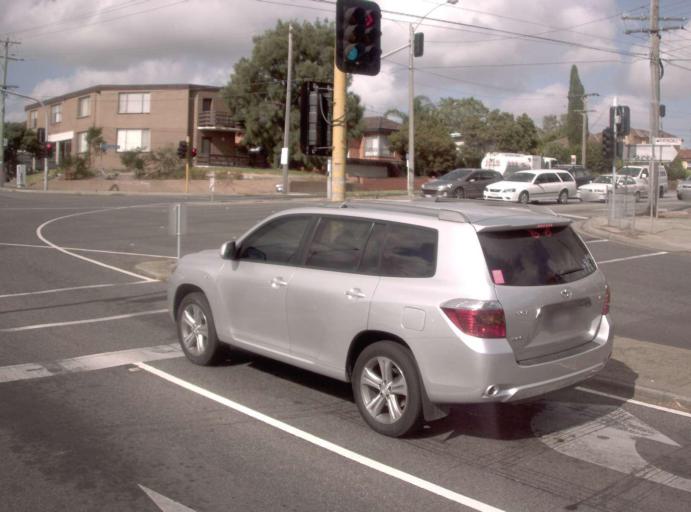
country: AU
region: Victoria
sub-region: Monash
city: Chadstone
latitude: -37.8968
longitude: 145.1063
